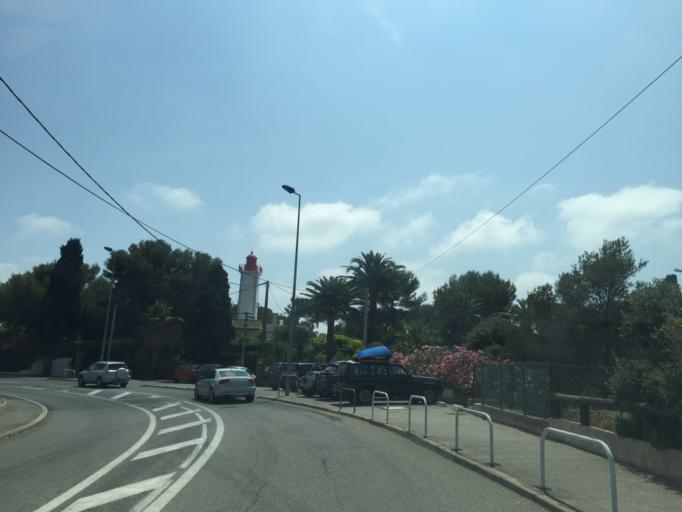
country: FR
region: Provence-Alpes-Cote d'Azur
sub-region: Departement du Var
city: Saint-Raphael
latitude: 43.4268
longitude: 6.8711
